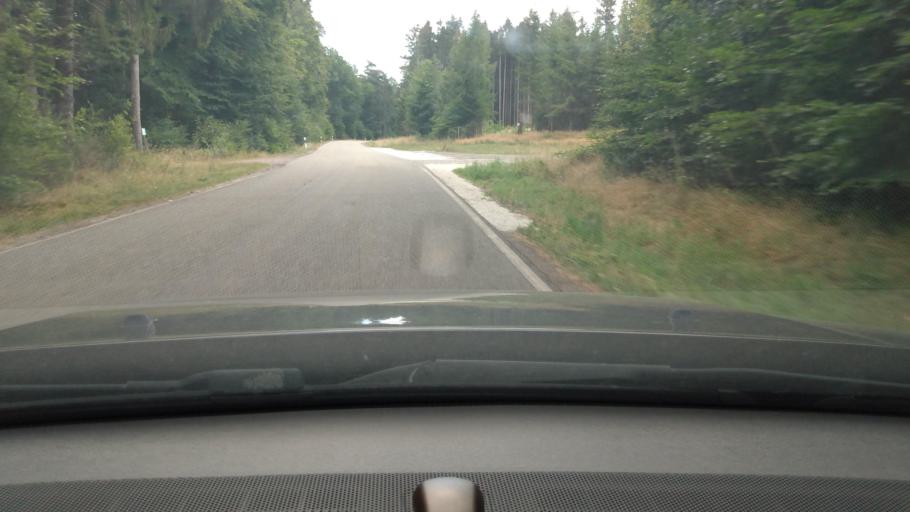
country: DE
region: Rheinland-Pfalz
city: Gornhausen
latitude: 49.8614
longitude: 7.0578
